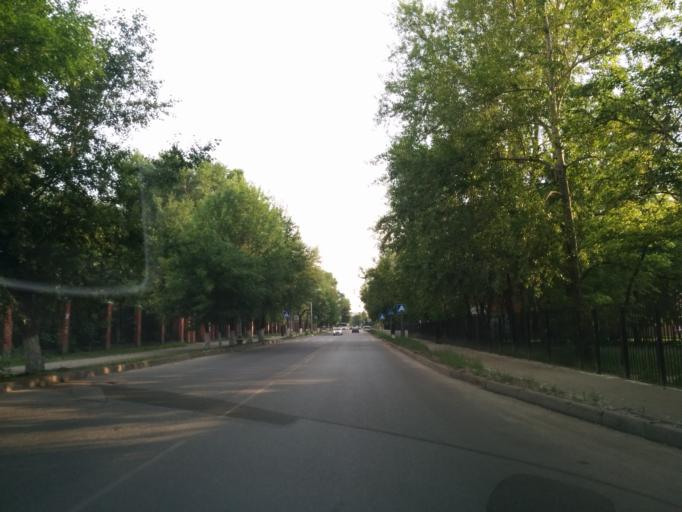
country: RU
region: Perm
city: Perm
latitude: 58.0246
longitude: 56.2938
